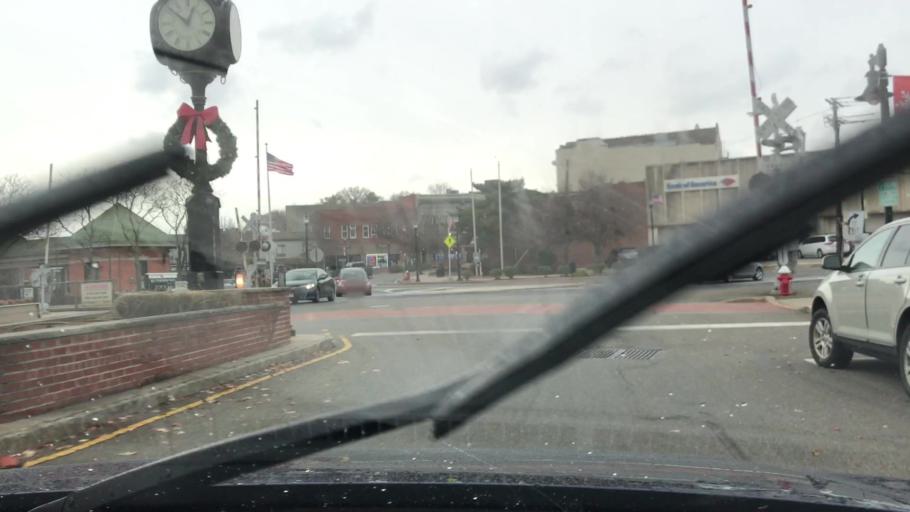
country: US
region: New Jersey
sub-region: Bergen County
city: East Rutherford
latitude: 40.8291
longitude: -74.1006
